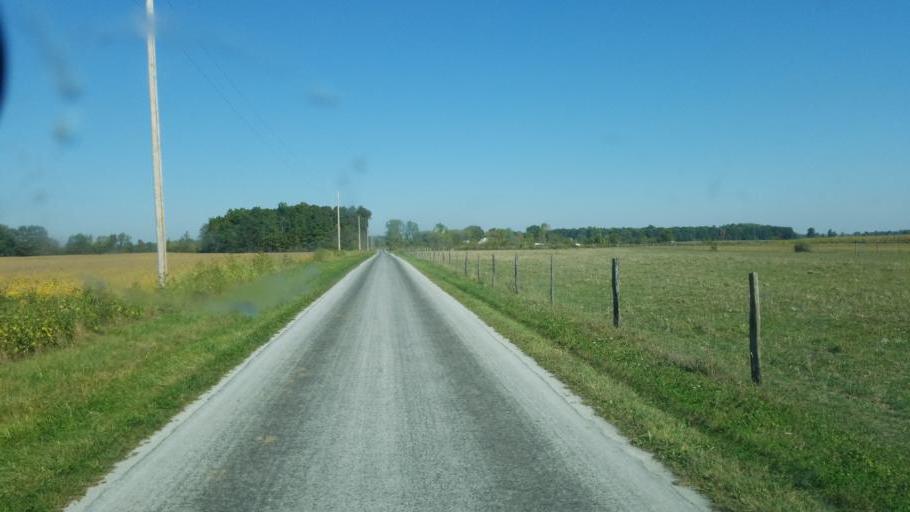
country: US
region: Ohio
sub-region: Hardin County
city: Kenton
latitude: 40.5702
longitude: -83.4879
